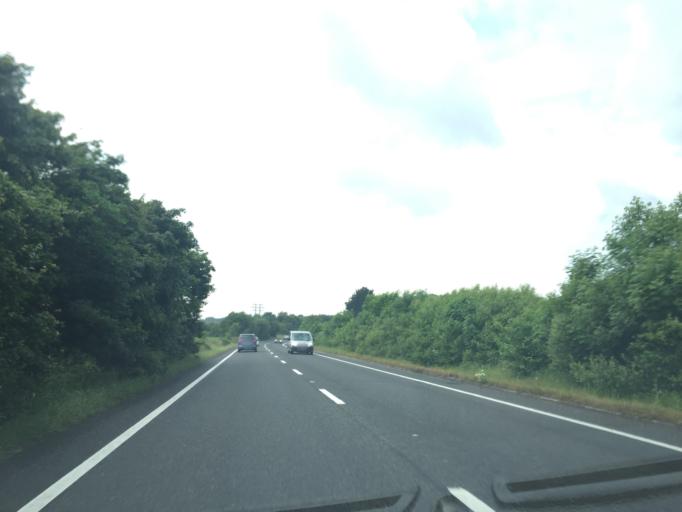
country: GB
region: England
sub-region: Dorset
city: Wareham
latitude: 50.6779
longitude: -2.1198
